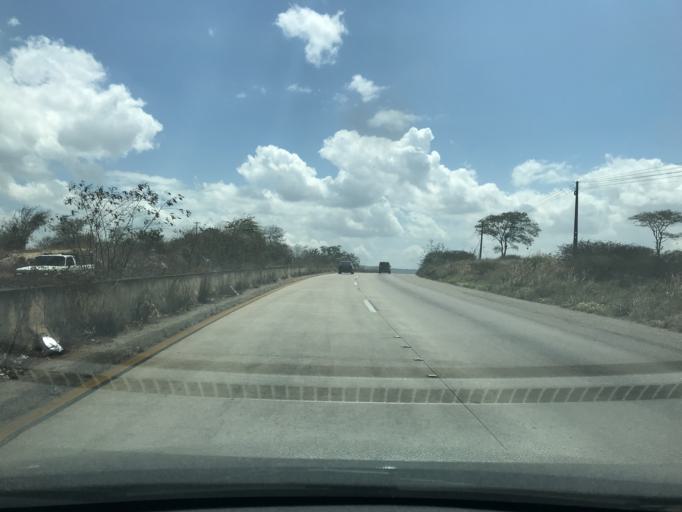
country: BR
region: Pernambuco
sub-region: Bezerros
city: Bezerros
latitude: -8.2968
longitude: -35.8293
